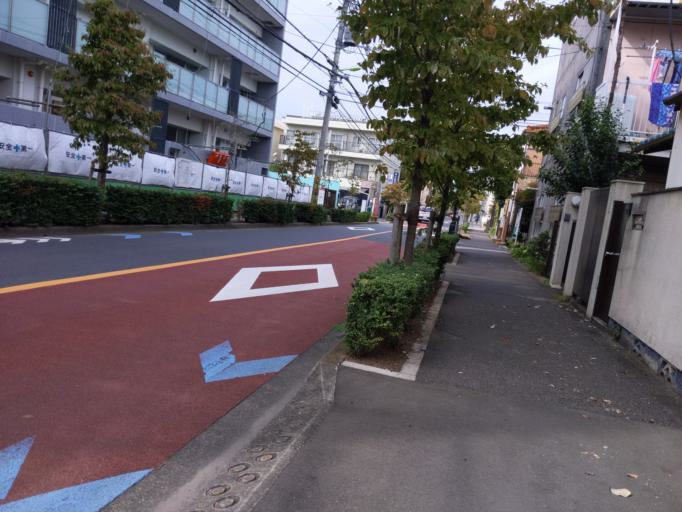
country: JP
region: Tokyo
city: Tokyo
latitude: 35.6504
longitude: 139.6287
